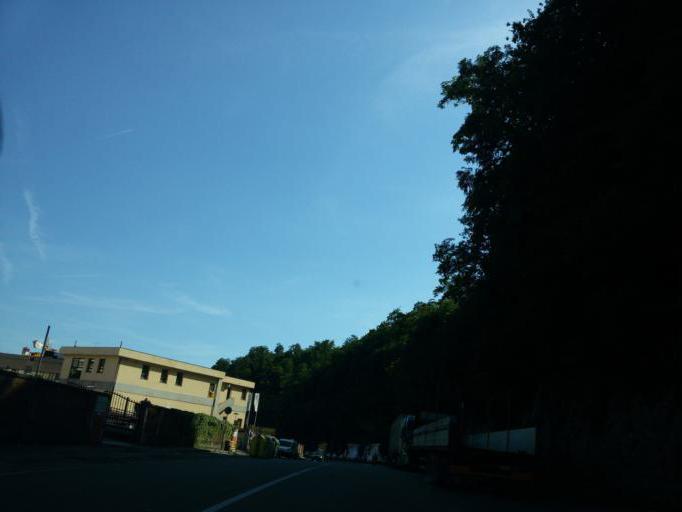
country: IT
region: Liguria
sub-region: Provincia di Genova
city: San Teodoro
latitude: 44.4222
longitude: 8.8793
